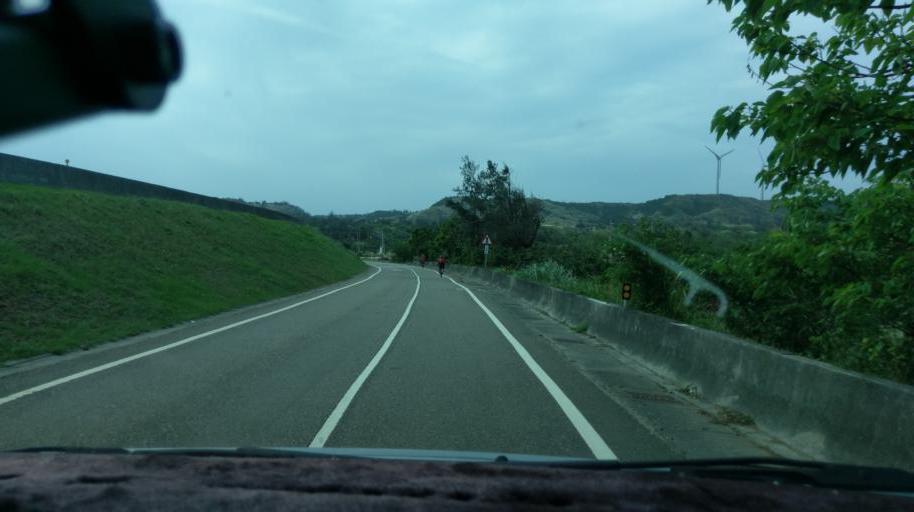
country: TW
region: Taiwan
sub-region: Miaoli
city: Miaoli
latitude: 24.6036
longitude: 120.7445
